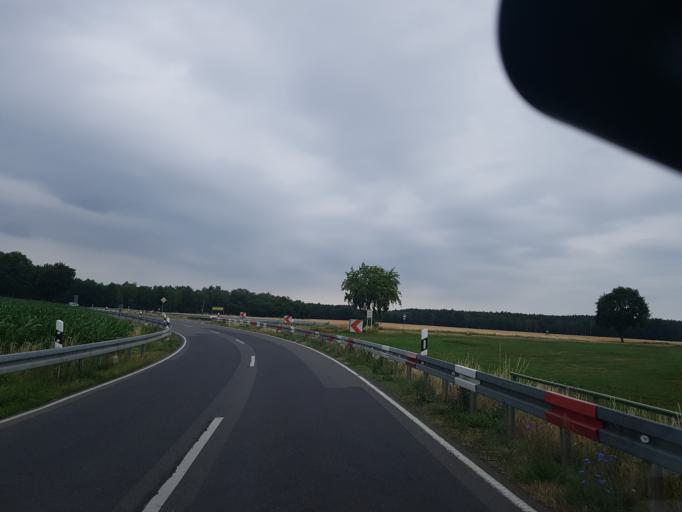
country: DE
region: Brandenburg
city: Lebusa
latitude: 51.8048
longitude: 13.4224
